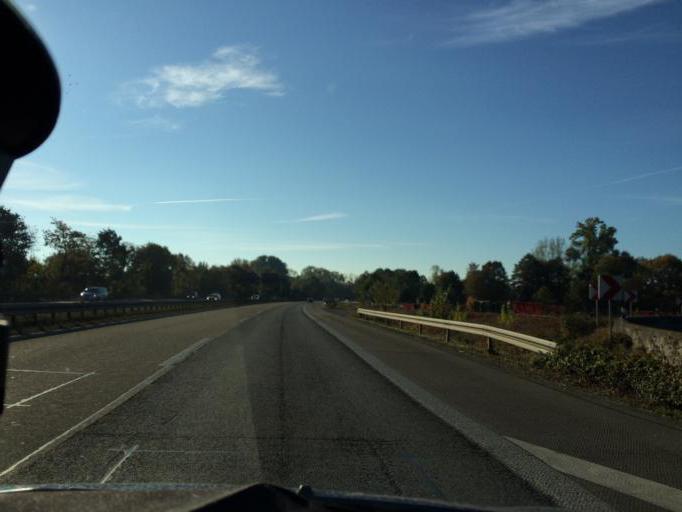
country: DE
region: North Rhine-Westphalia
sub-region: Regierungsbezirk Koln
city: Troisdorf
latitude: 50.7899
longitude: 7.1494
